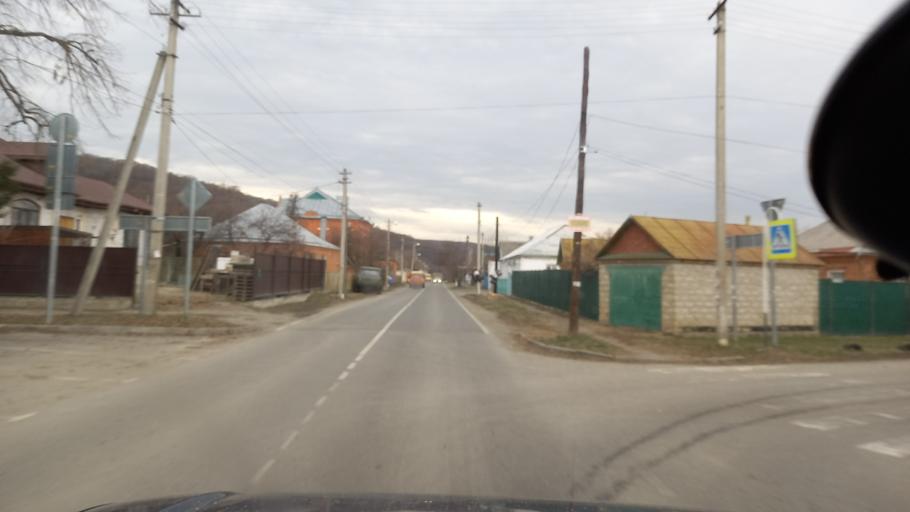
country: RU
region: Adygeya
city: Maykop
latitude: 44.5923
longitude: 40.1026
